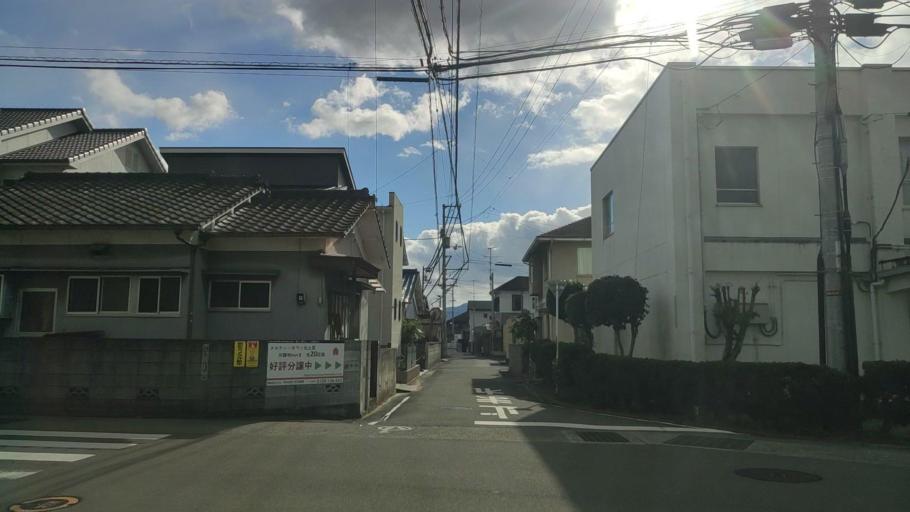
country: JP
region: Ehime
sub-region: Shikoku-chuo Shi
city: Matsuyama
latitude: 33.8092
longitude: 132.7845
